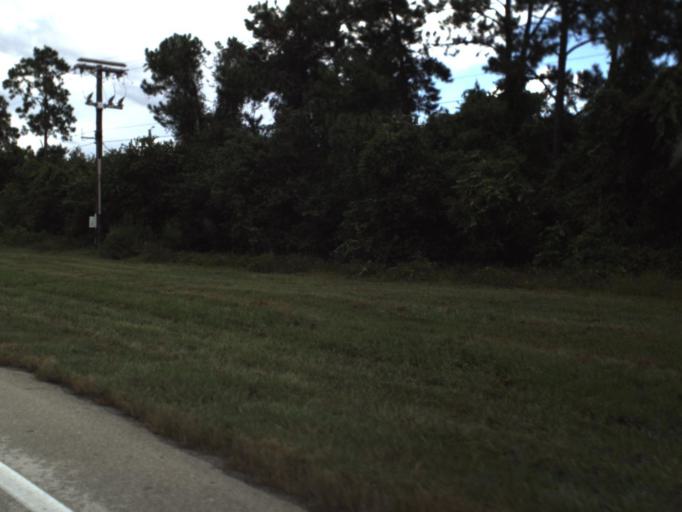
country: US
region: Florida
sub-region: Polk County
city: Mulberry
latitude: 27.8242
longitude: -81.9804
